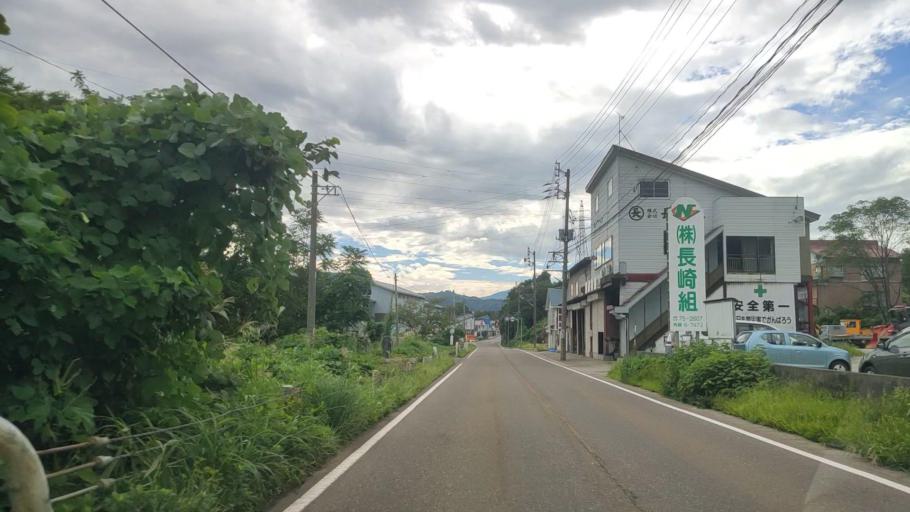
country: JP
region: Niigata
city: Arai
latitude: 36.9943
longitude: 138.2692
